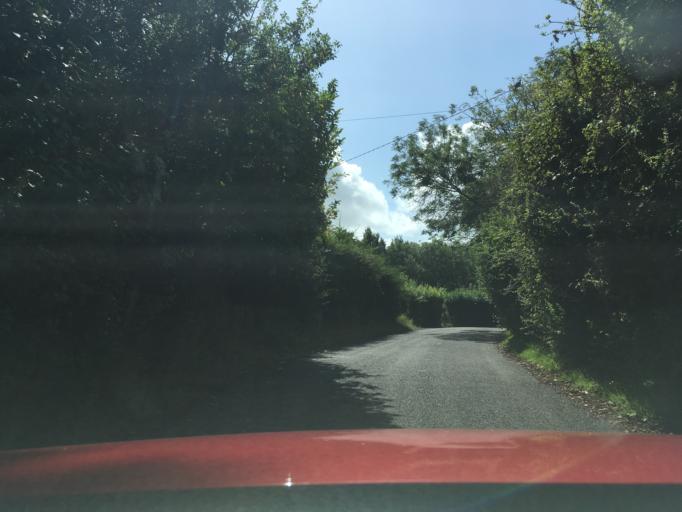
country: GB
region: England
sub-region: West Berkshire
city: Wickham
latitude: 51.4236
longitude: -1.4124
